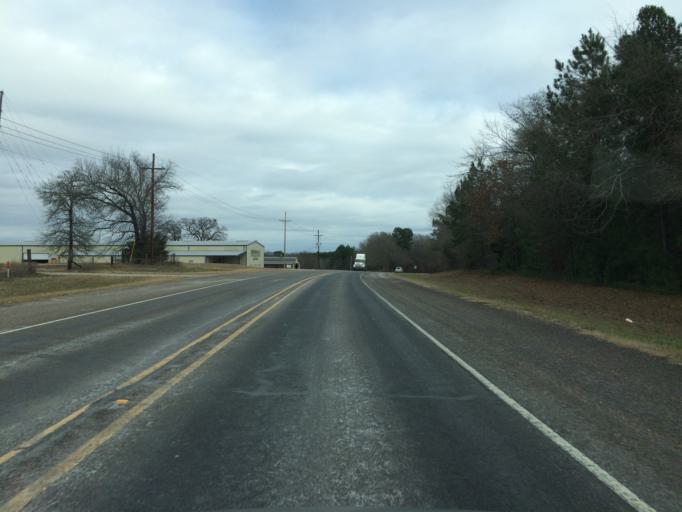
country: US
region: Texas
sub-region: Wood County
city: Mineola
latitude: 32.6882
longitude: -95.4744
